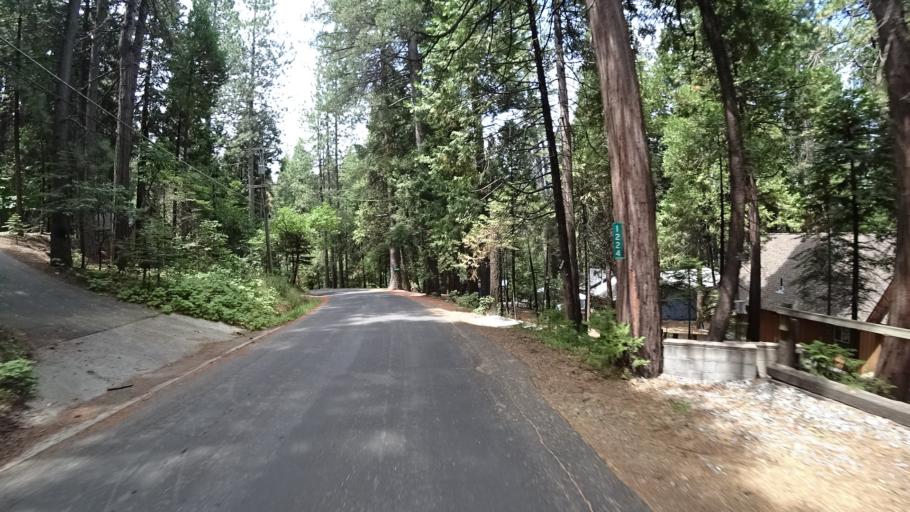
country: US
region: California
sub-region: Calaveras County
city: Arnold
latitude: 38.2536
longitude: -120.3499
